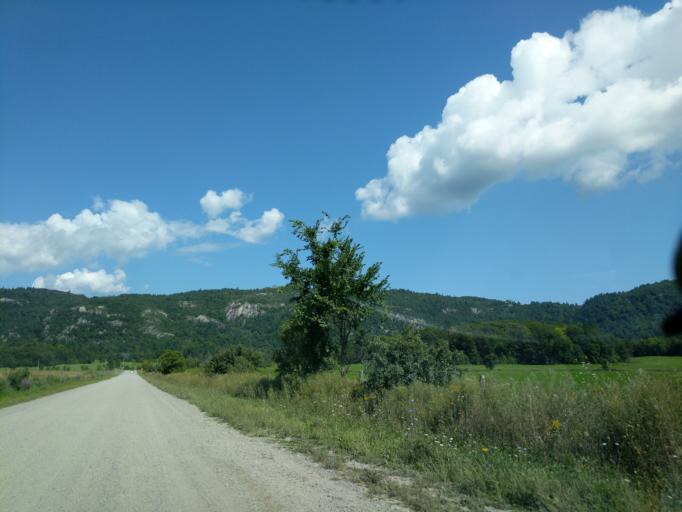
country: CA
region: Quebec
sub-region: Outaouais
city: Wakefield
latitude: 45.5134
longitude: -75.9547
